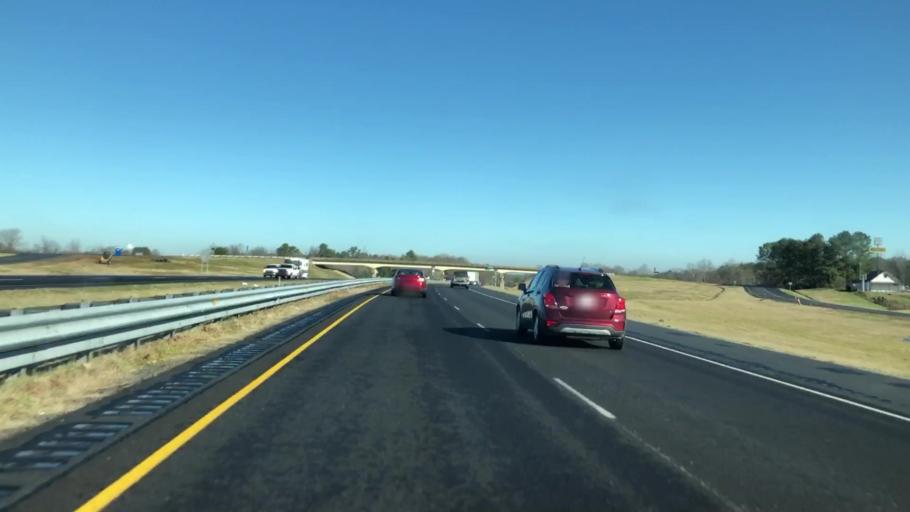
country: US
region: Alabama
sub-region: Limestone County
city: Ardmore
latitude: 34.9707
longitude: -86.8846
